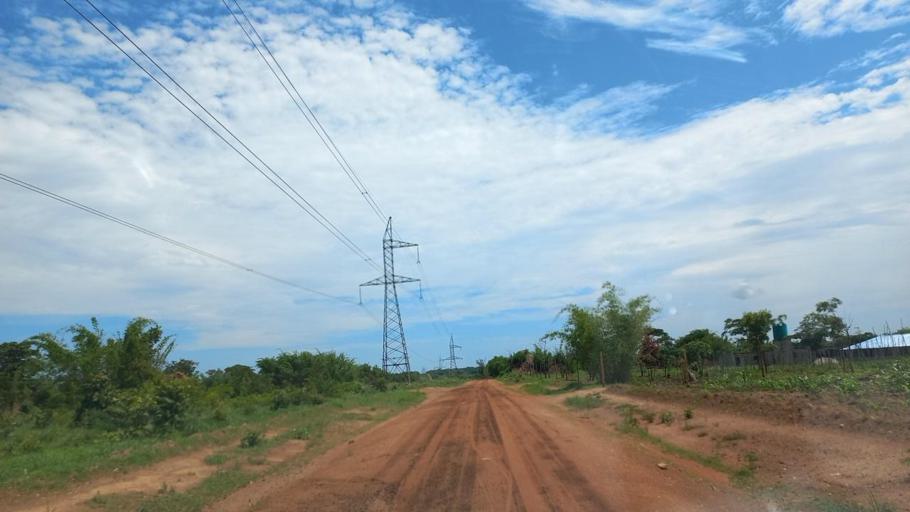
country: ZM
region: Copperbelt
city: Kitwe
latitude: -12.8193
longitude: 28.3541
